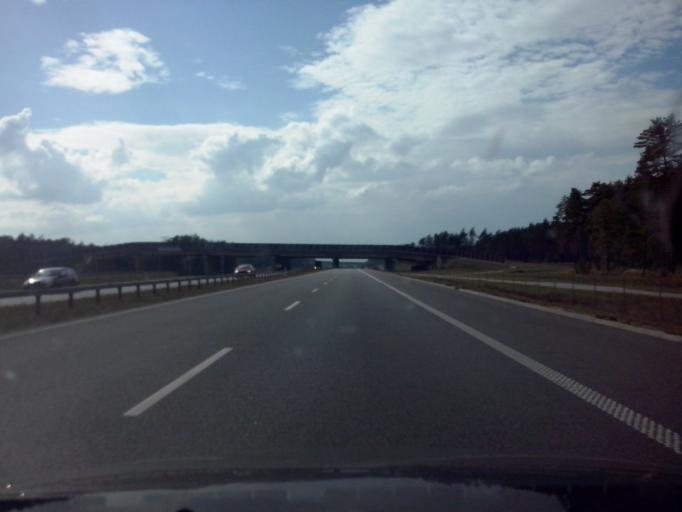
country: PL
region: Lesser Poland Voivodeship
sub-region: Powiat tarnowski
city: Wierzchoslawice
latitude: 50.0072
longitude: 20.8210
